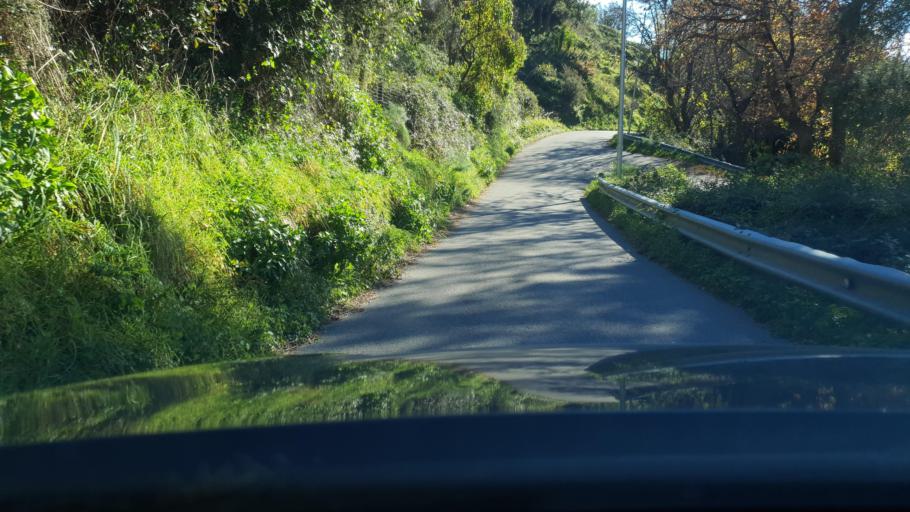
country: IT
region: Calabria
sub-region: Provincia di Catanzaro
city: Sant'Elia
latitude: 38.9598
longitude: 16.5785
